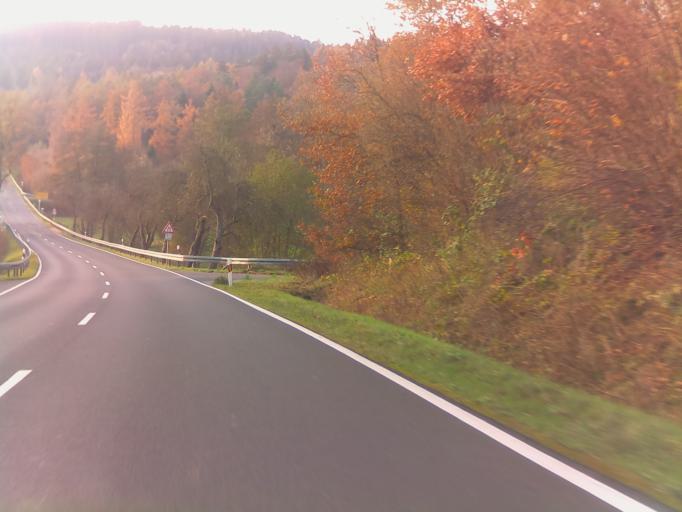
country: DE
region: Bavaria
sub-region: Regierungsbezirk Unterfranken
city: Zeitlofs
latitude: 50.2633
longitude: 9.6505
